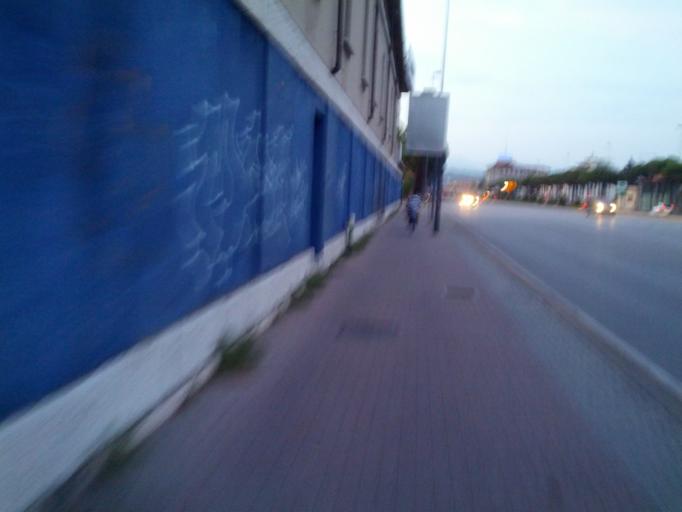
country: IT
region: Veneto
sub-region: Provincia di Verona
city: Verona
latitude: 45.4251
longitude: 10.9847
